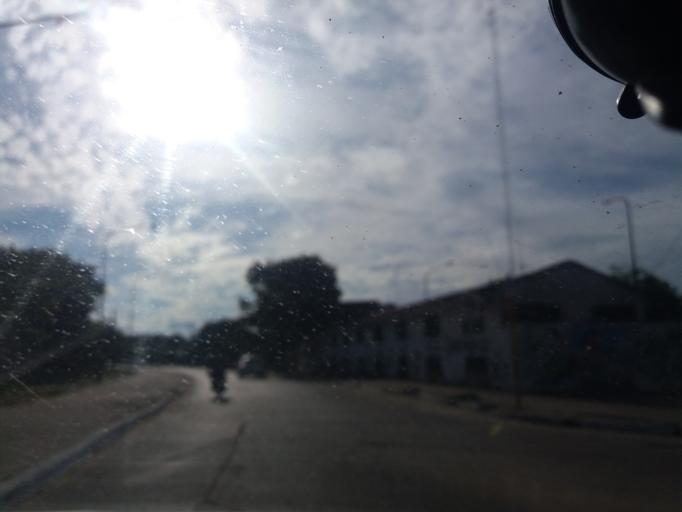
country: AR
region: Corrientes
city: Corrientes
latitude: -27.4829
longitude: -58.8262
